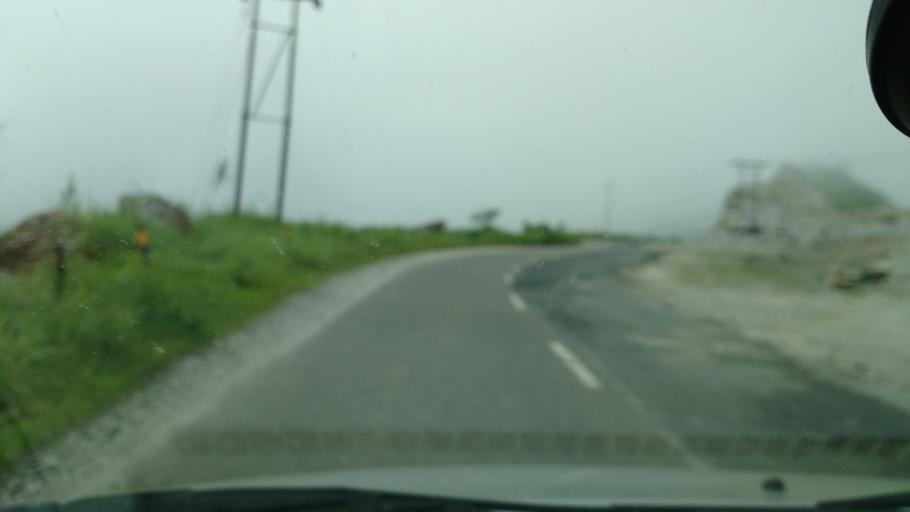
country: IN
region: Meghalaya
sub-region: East Khasi Hills
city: Cherrapunji
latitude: 25.3674
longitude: 91.8768
